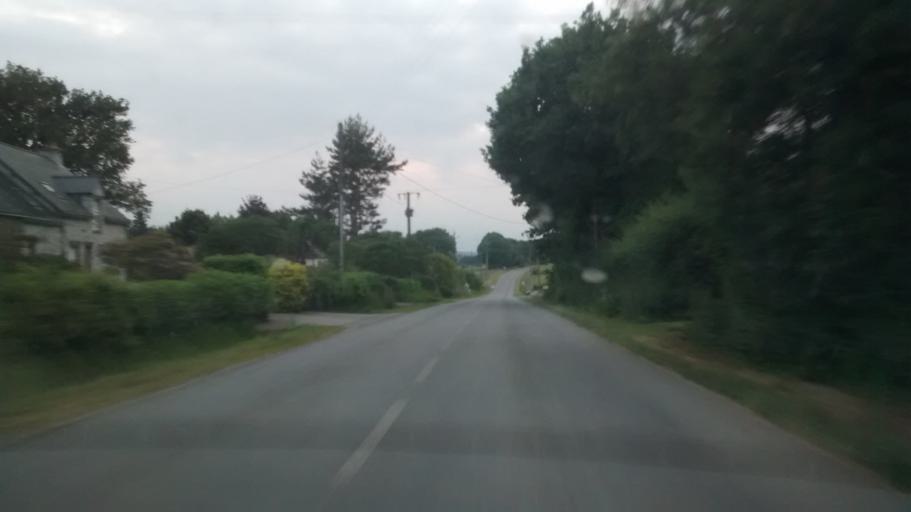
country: FR
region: Brittany
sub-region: Departement du Morbihan
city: Saint-Martin-sur-Oust
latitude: 47.7424
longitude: -2.2336
